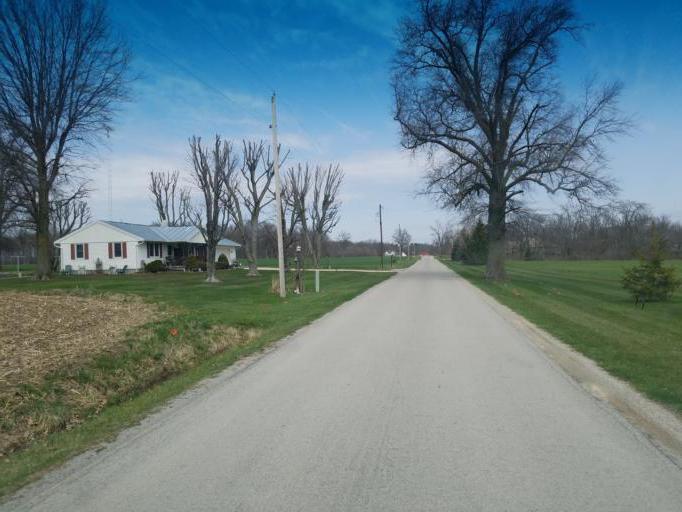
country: US
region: Ohio
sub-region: Wyandot County
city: Upper Sandusky
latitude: 40.8576
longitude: -83.2562
